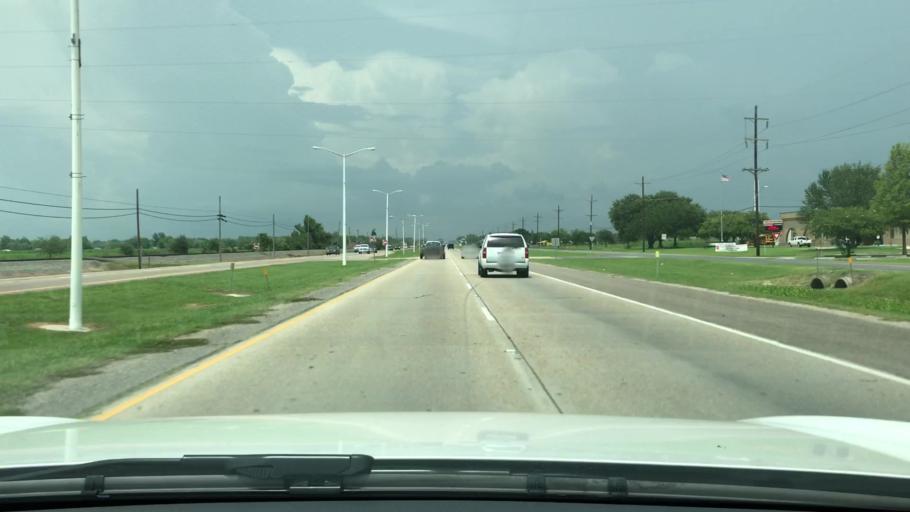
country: US
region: Louisiana
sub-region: West Baton Rouge Parish
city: Brusly
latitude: 30.3925
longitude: -91.2405
